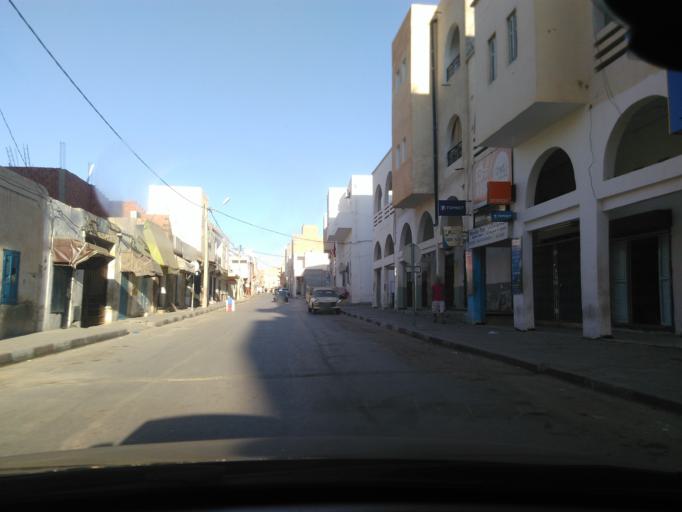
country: TN
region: Tataouine
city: Tataouine
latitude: 32.9278
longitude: 10.4471
